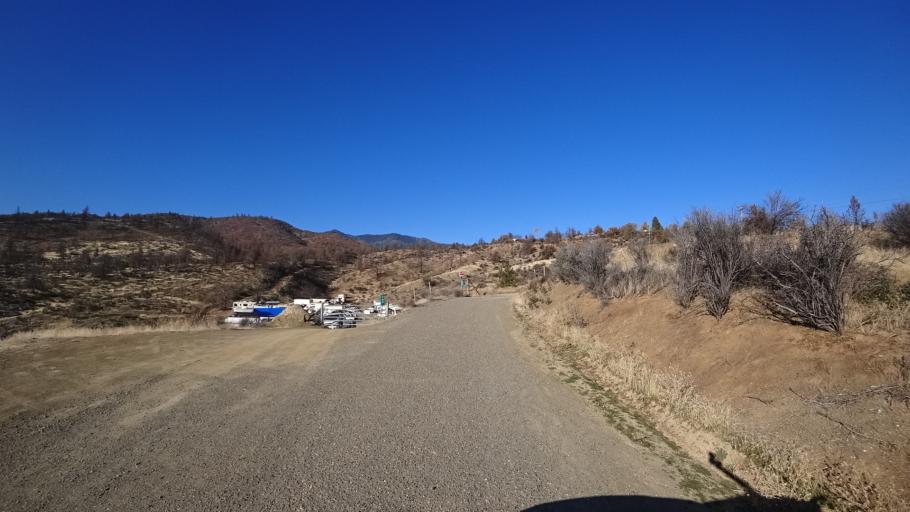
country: US
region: California
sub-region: Siskiyou County
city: Montague
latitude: 41.9020
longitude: -122.5695
